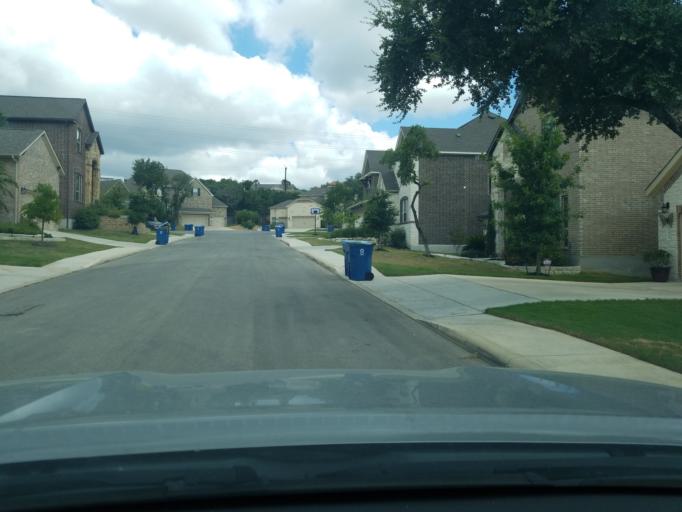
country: US
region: Texas
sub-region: Bexar County
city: Timberwood Park
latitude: 29.6670
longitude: -98.5100
